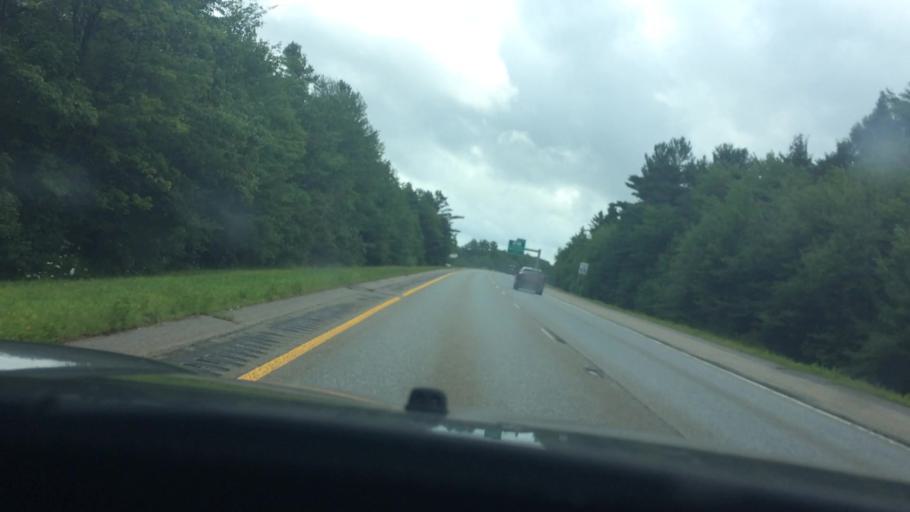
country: US
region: Massachusetts
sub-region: Worcester County
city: Templeton
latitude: 42.5673
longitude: -72.0640
